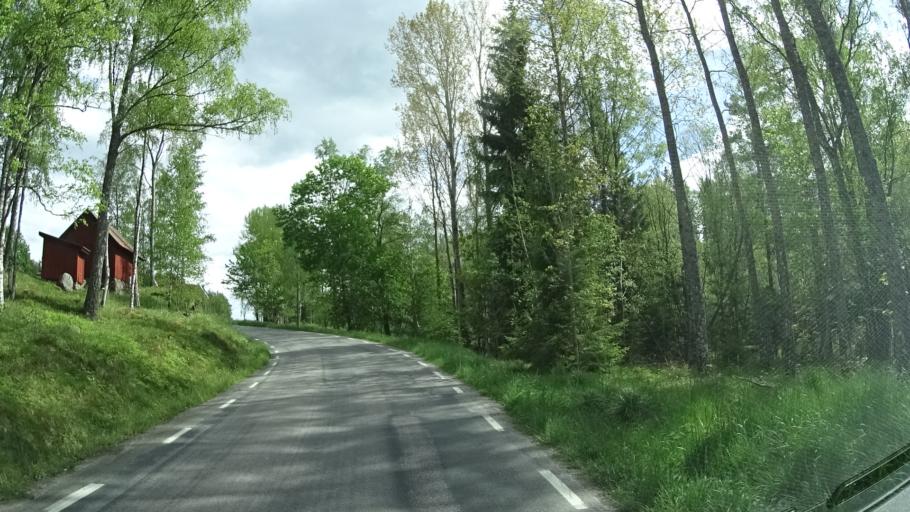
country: SE
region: OEstergoetland
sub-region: Finspangs Kommun
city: Finspang
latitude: 58.6085
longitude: 15.7400
